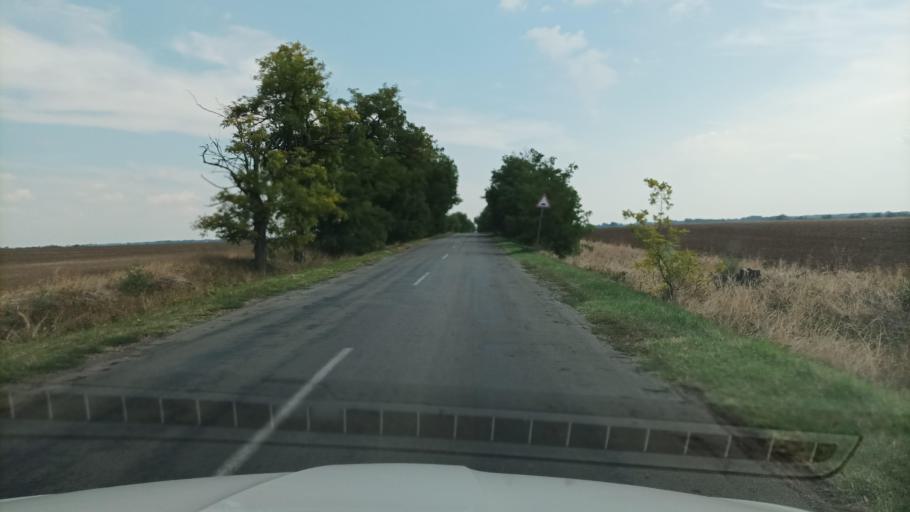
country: HU
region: Pest
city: Tura
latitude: 47.6211
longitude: 19.6274
